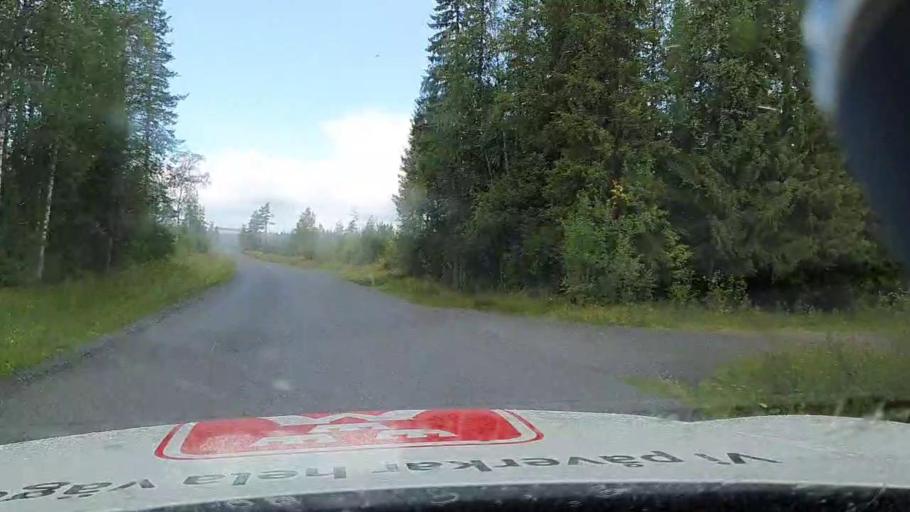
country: SE
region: Jaemtland
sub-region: Stroemsunds Kommun
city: Stroemsund
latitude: 63.8785
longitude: 15.3539
